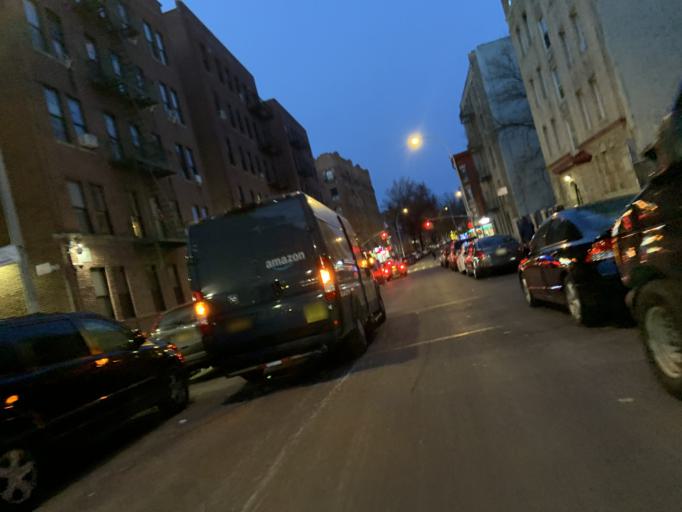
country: US
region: New York
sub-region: Bronx
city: The Bronx
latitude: 40.8644
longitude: -73.8932
